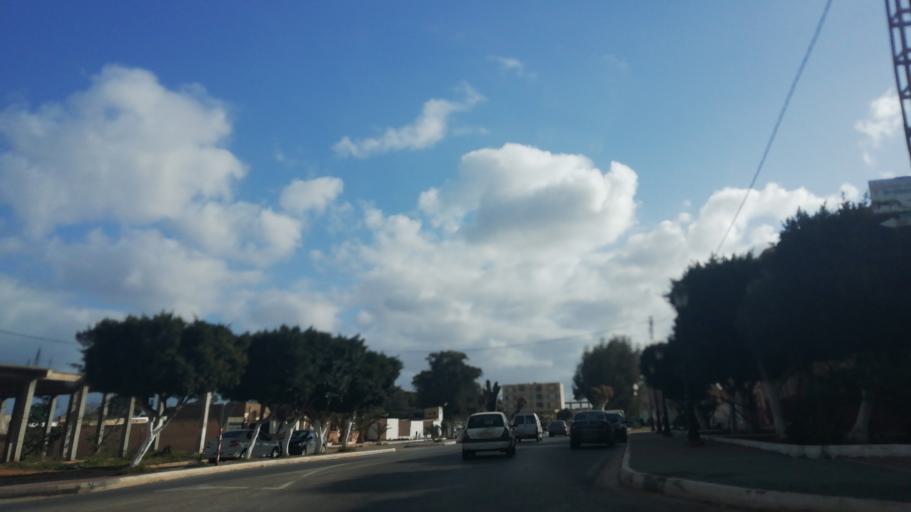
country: DZ
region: Relizane
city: Mazouna
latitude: 36.2529
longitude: 0.5686
